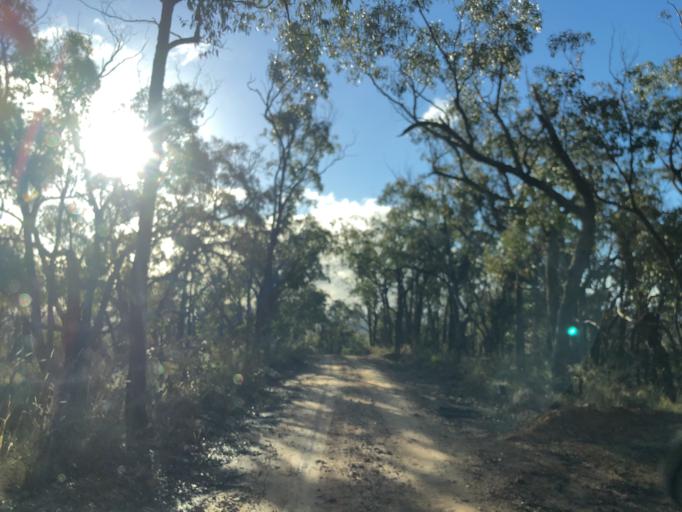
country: AU
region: Victoria
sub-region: Mount Alexander
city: Castlemaine
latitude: -37.2309
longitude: 144.2688
